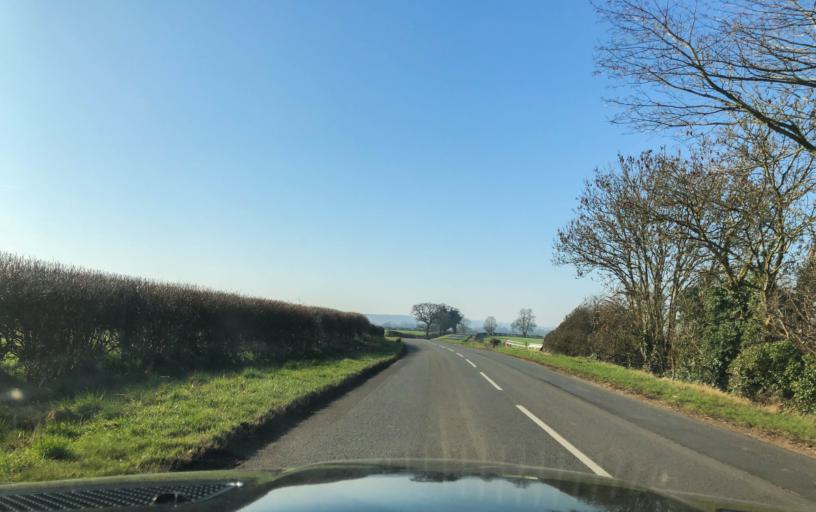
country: GB
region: England
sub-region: Warwickshire
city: Wellesbourne Mountford
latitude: 52.2071
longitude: -1.5785
